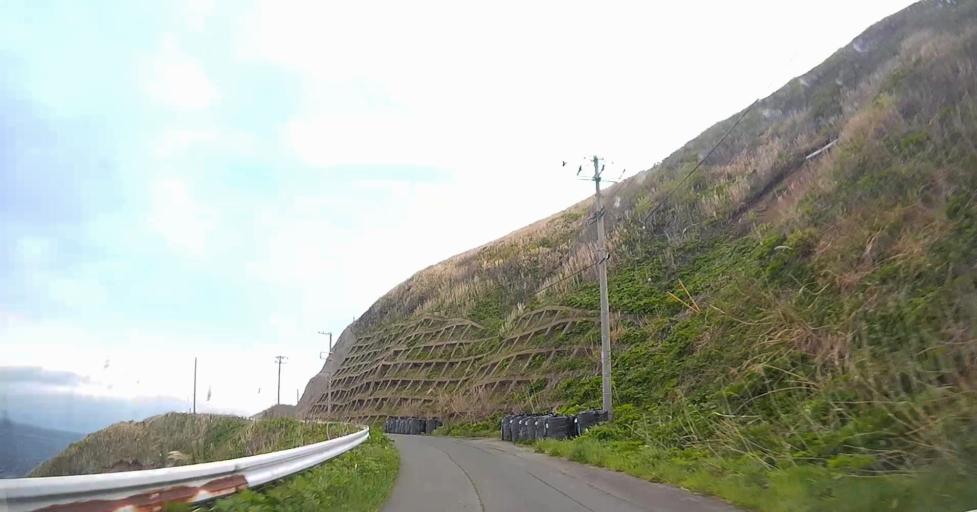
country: JP
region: Aomori
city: Shimokizukuri
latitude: 41.2481
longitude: 140.3435
